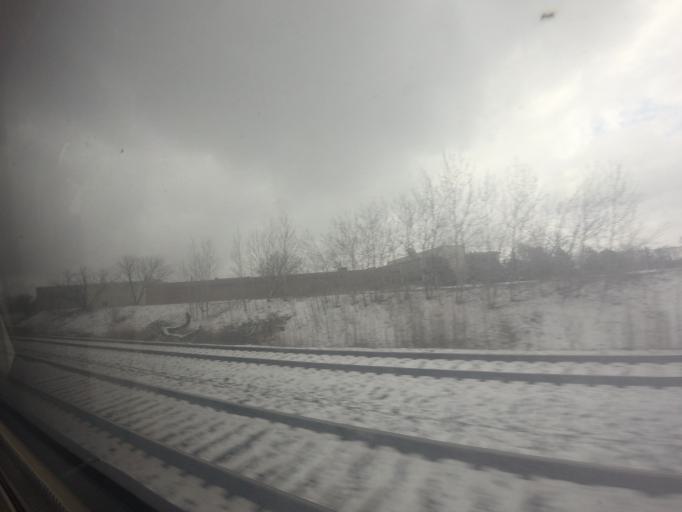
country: CA
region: Ontario
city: Scarborough
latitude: 43.6976
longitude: -79.2680
